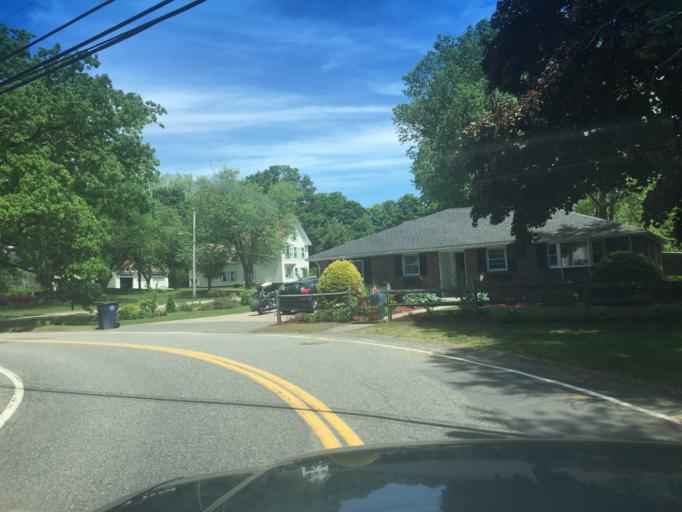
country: US
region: Massachusetts
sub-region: Norfolk County
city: Medway
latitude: 42.1409
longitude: -71.4216
